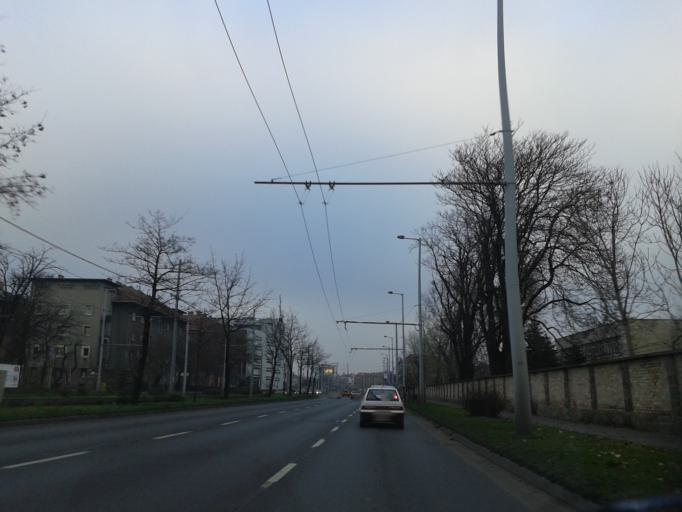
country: HU
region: Budapest
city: Budapest XIV. keruelet
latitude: 47.4972
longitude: 19.1092
